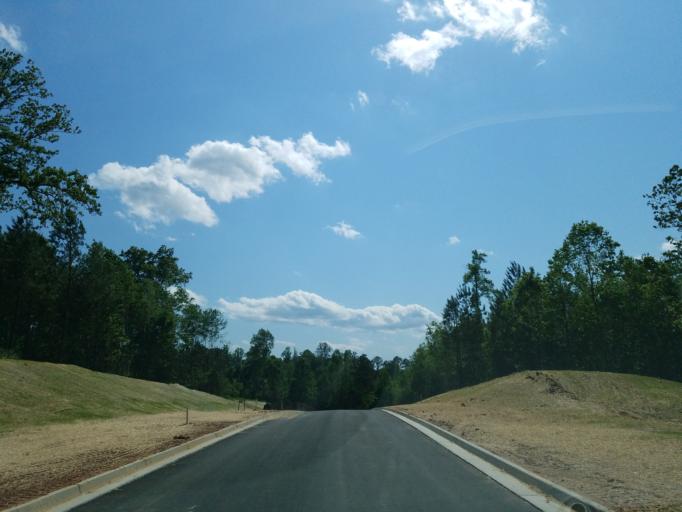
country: US
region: Georgia
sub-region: Fulton County
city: Milton
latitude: 34.2085
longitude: -84.2860
